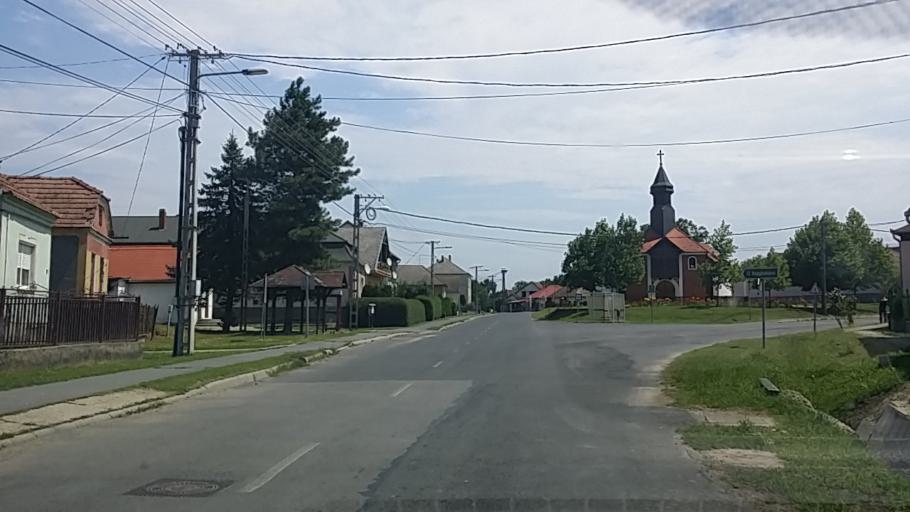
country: HR
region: Medimurska
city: Kotoriba
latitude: 46.3852
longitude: 16.8302
